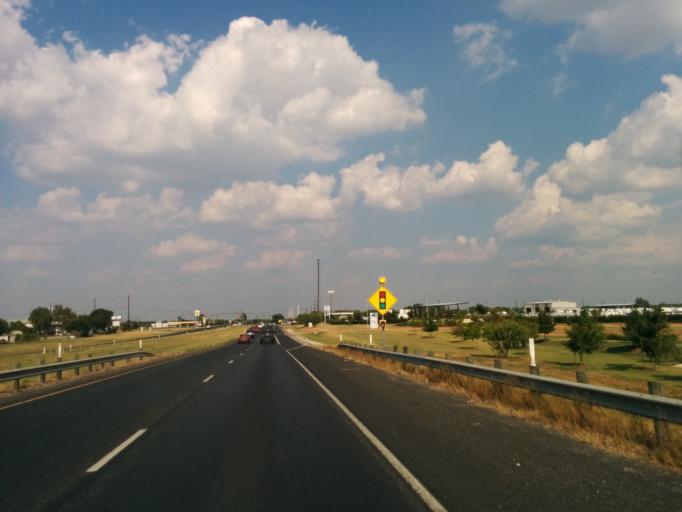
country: US
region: Texas
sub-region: Bexar County
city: Elmendorf
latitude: 29.3076
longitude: -98.3977
